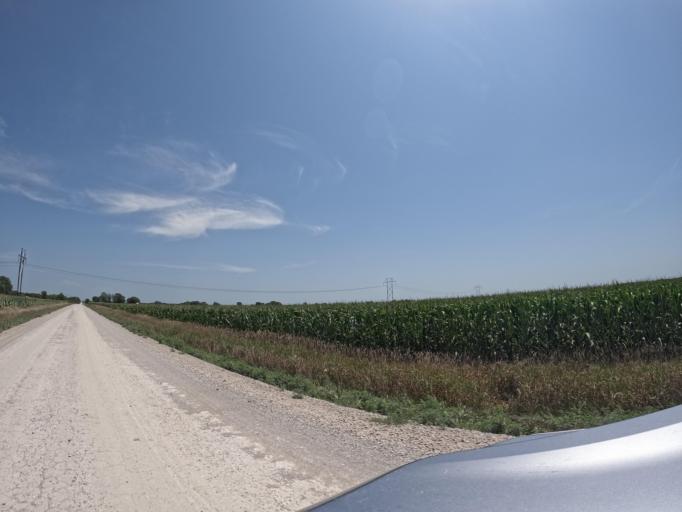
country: US
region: Iowa
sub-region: Henry County
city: Mount Pleasant
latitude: 40.9086
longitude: -91.6409
